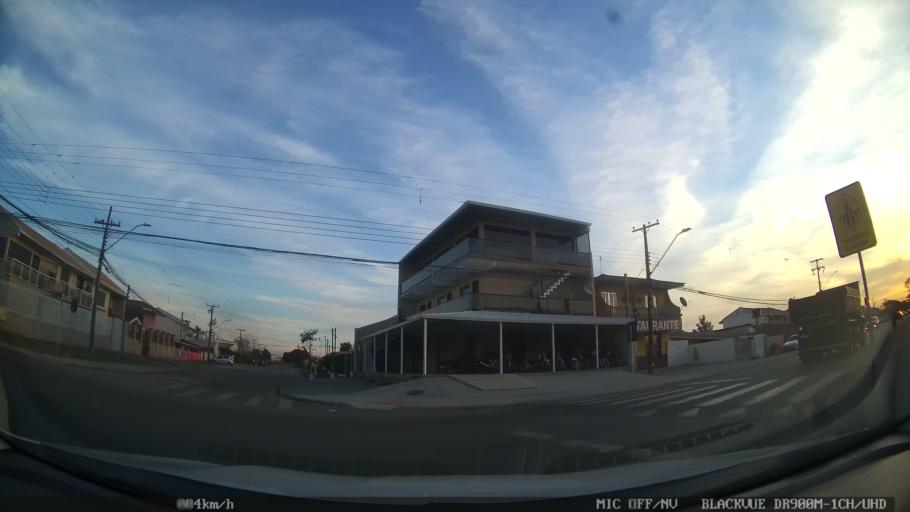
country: BR
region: Parana
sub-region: Pinhais
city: Pinhais
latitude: -25.4655
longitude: -49.1879
